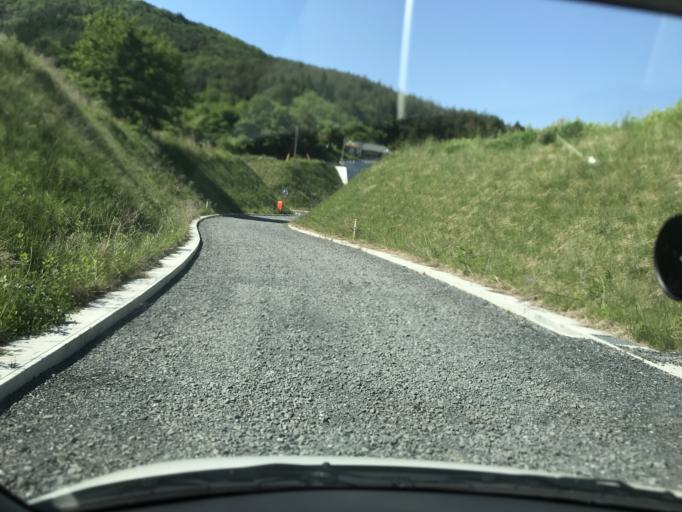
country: JP
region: Iwate
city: Ichinoseki
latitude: 38.9870
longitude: 141.2150
